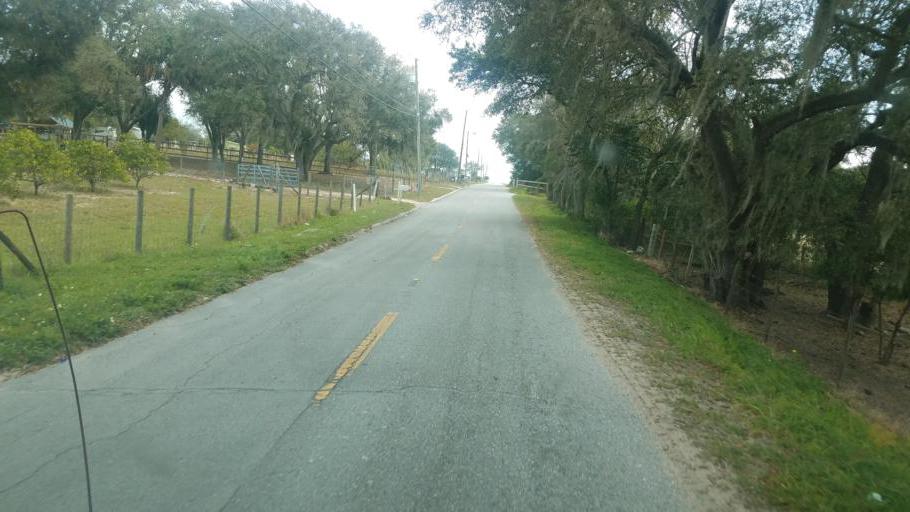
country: US
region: Florida
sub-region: Polk County
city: Dundee
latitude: 28.0334
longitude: -81.6068
